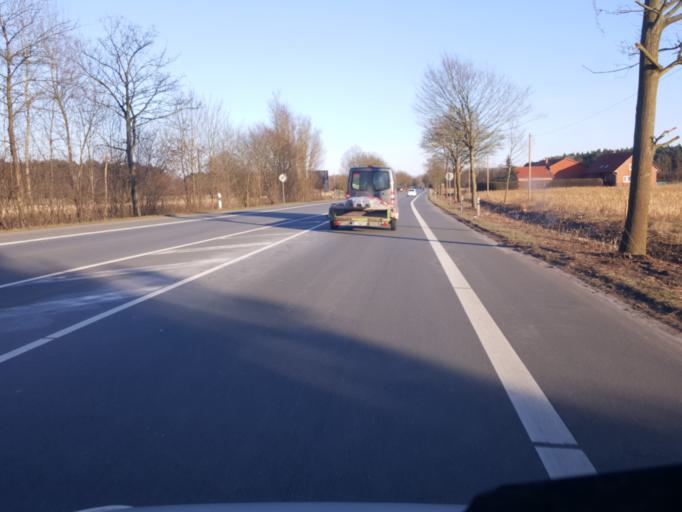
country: DE
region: North Rhine-Westphalia
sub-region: Regierungsbezirk Detmold
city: Hille
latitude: 52.3940
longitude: 8.7069
